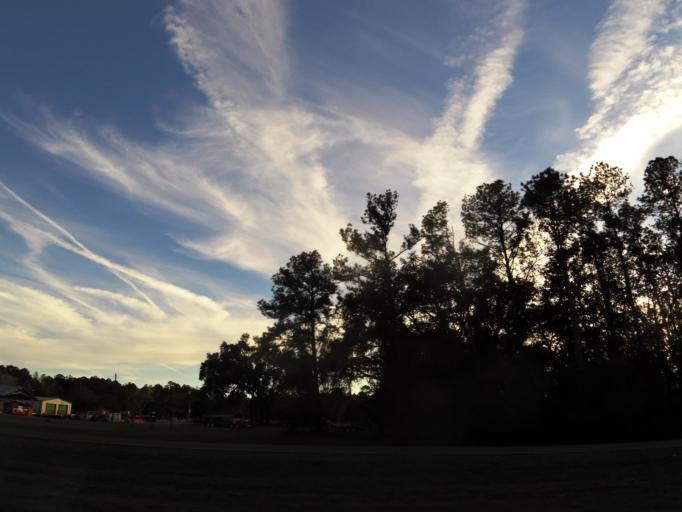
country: US
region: Florida
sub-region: Baker County
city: Macclenny
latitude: 30.2598
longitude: -82.1333
